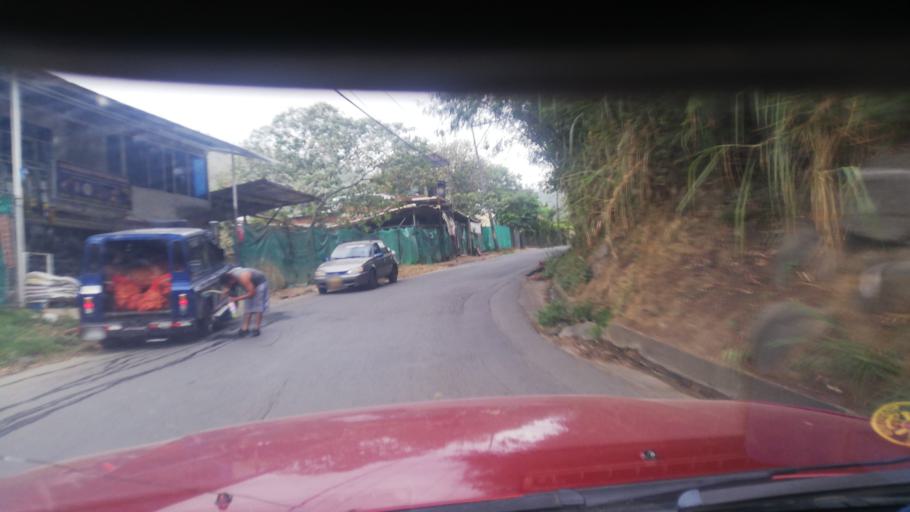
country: CO
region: Valle del Cauca
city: Cali
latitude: 3.4790
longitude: -76.5534
